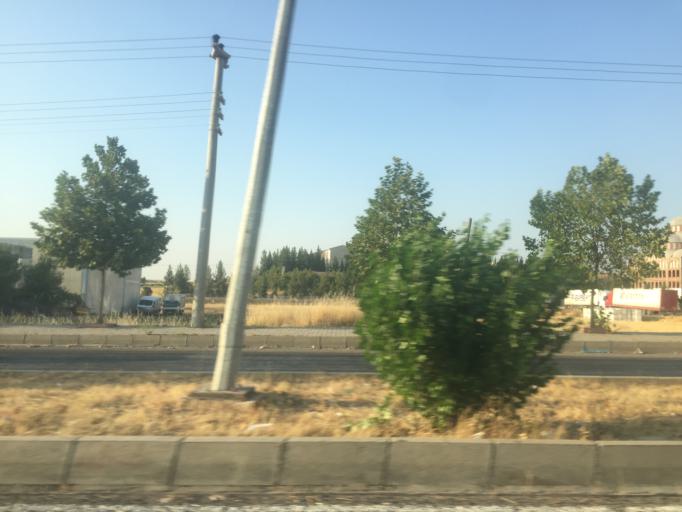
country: TR
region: Mardin
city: Midyat
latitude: 37.4350
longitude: 41.3250
